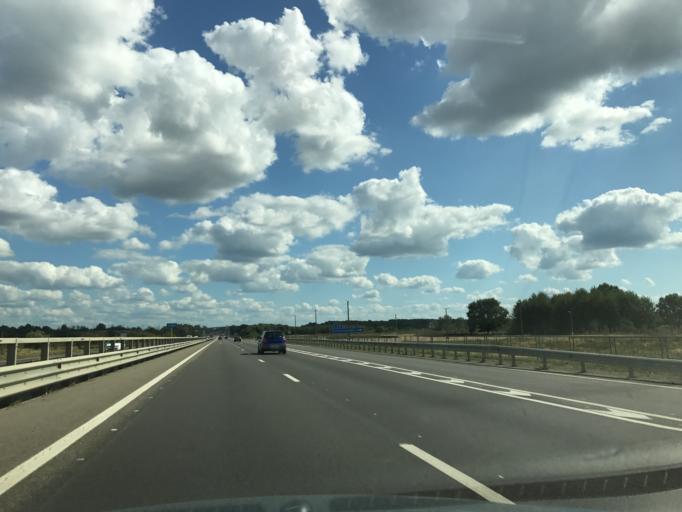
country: RU
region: Adygeya
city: Adygeysk
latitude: 44.8365
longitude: 39.2154
